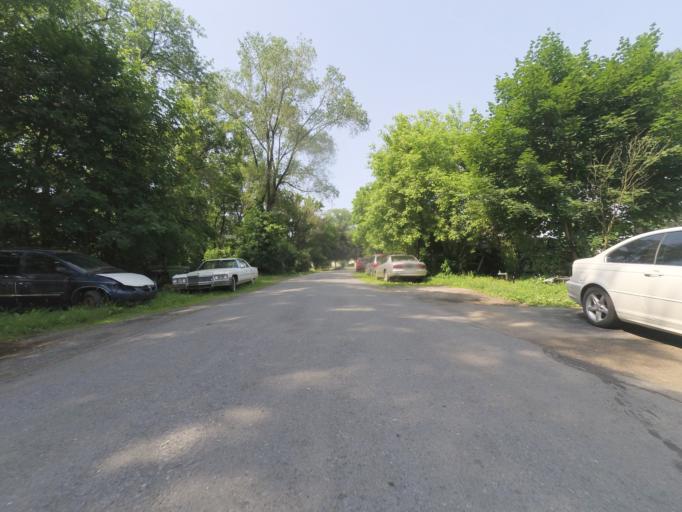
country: US
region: Pennsylvania
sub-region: Centre County
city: Milesburg
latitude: 40.9464
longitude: -77.7740
